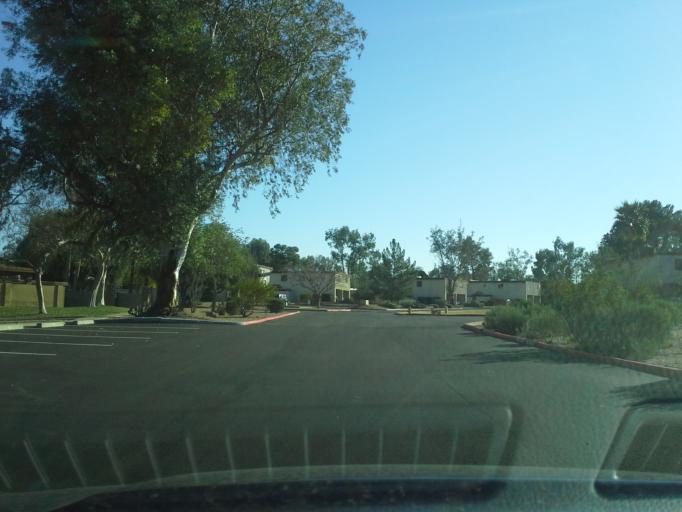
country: US
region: Arizona
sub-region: Maricopa County
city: Glendale
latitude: 33.6088
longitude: -112.0634
